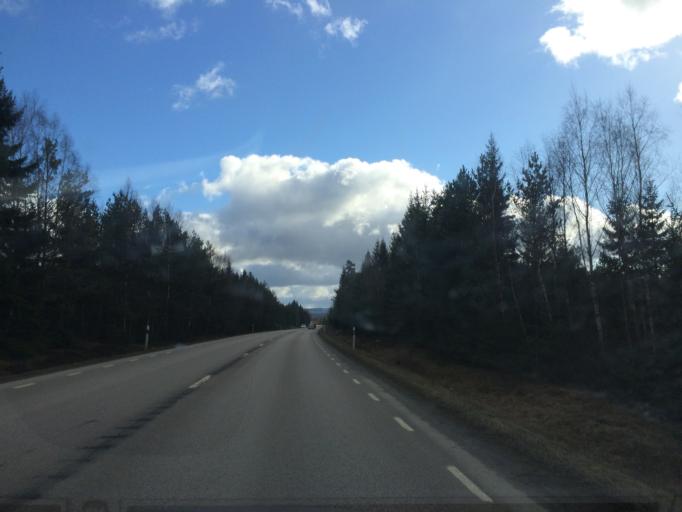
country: SE
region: Vaestra Goetaland
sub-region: Skara Kommun
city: Skara
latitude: 58.3046
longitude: 13.4670
